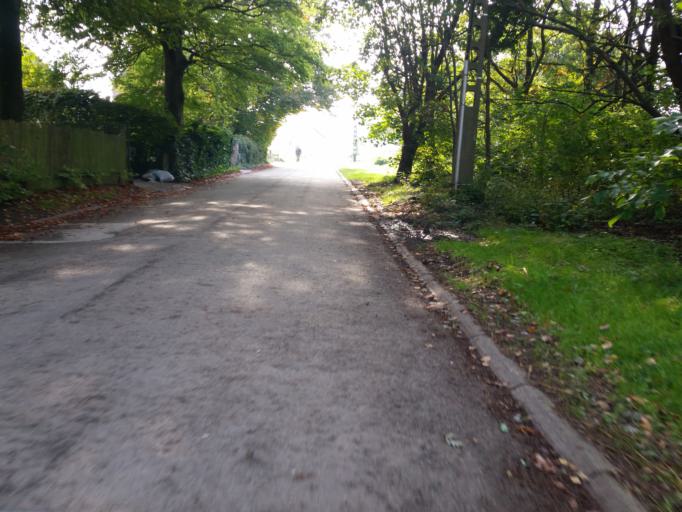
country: BE
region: Flanders
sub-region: Provincie Antwerpen
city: Mechelen
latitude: 51.0072
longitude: 4.5028
